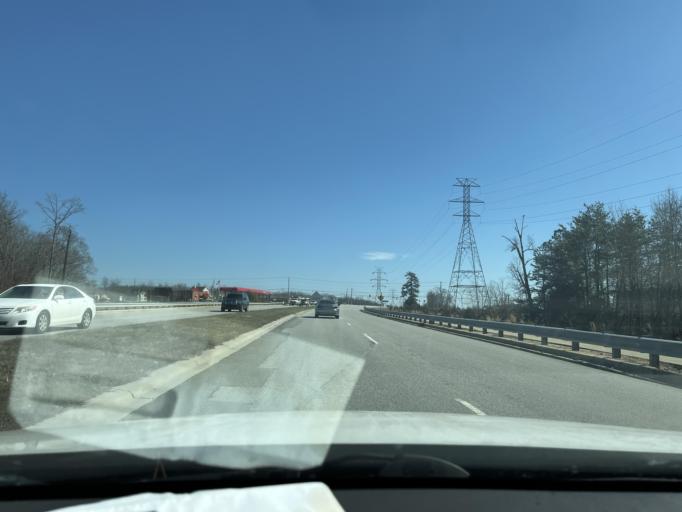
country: US
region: North Carolina
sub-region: Guilford County
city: Jamestown
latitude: 36.0024
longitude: -79.9108
